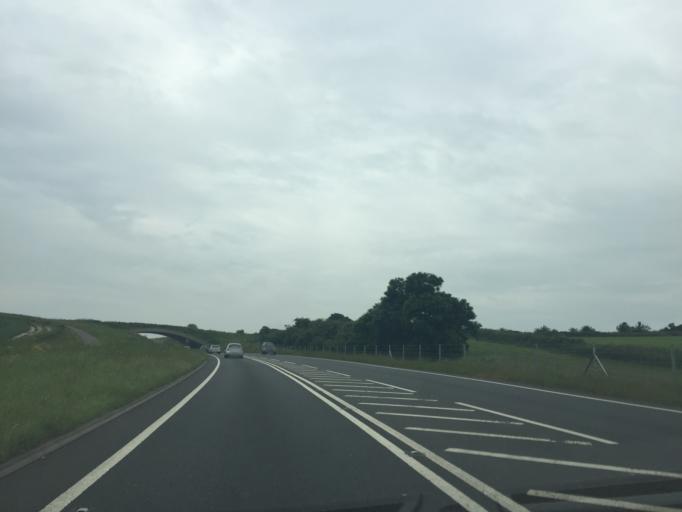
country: GB
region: England
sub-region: Dorset
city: Overcombe
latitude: 50.6743
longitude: -2.4661
